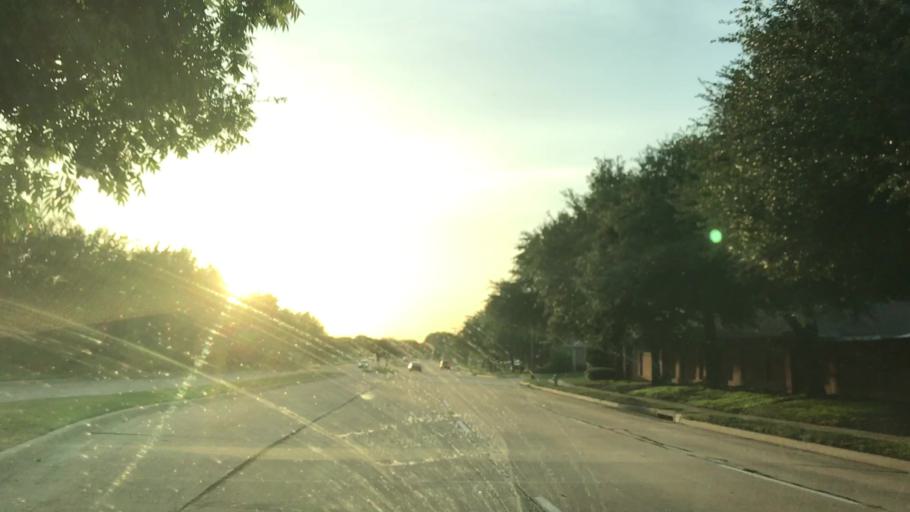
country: US
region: Texas
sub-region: Dallas County
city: Farmers Branch
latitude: 32.9220
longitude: -96.9526
